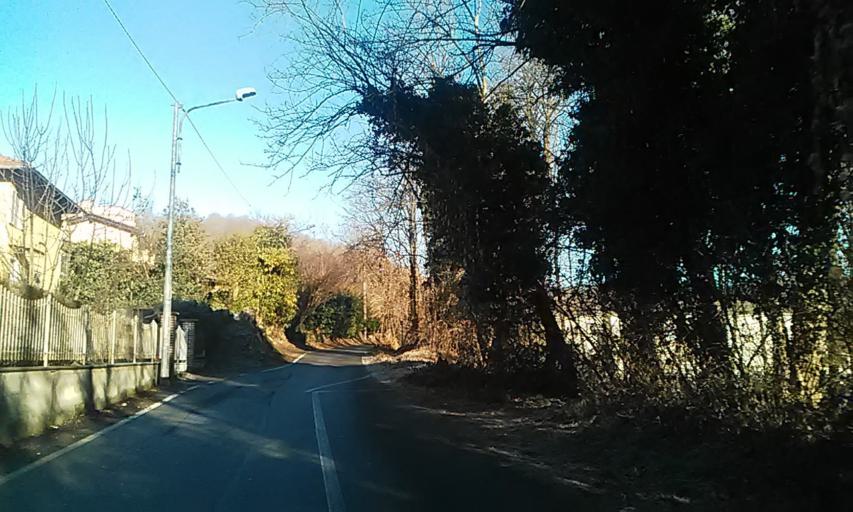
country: IT
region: Piedmont
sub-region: Provincia di Vercelli
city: Borgosesia
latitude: 45.7108
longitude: 8.2980
